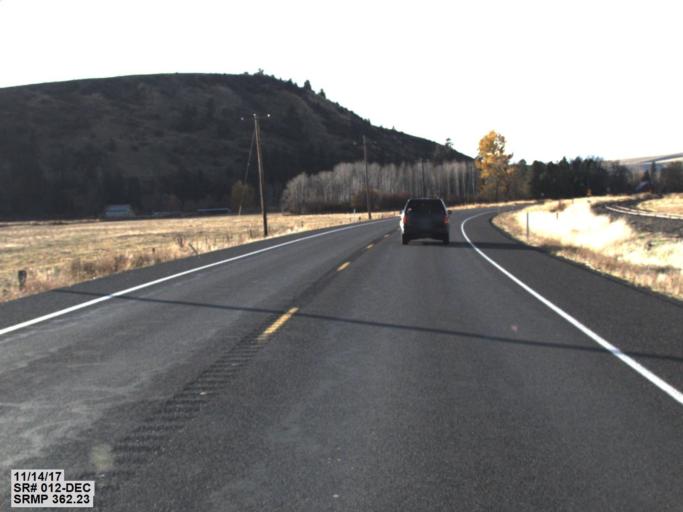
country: US
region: Washington
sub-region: Walla Walla County
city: Waitsburg
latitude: 46.2867
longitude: -118.0661
